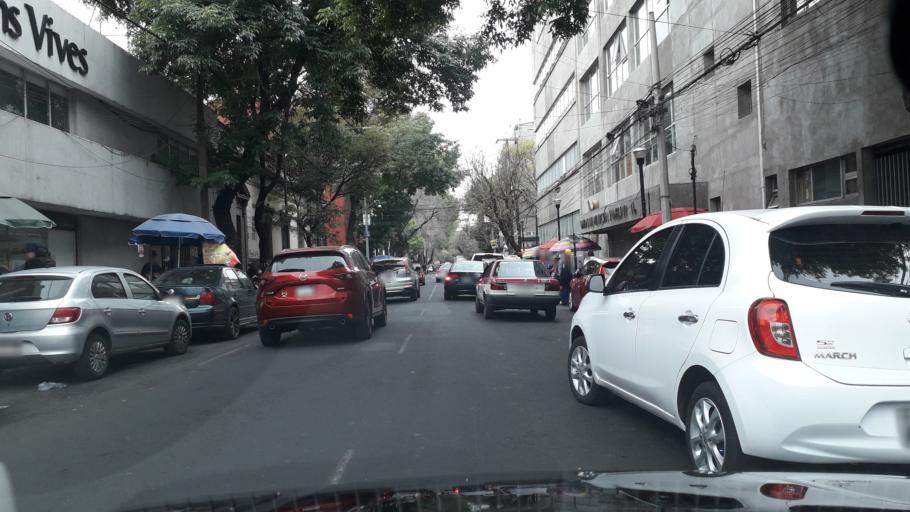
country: MX
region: Mexico City
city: Cuauhtemoc
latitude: 19.4453
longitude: -99.1588
